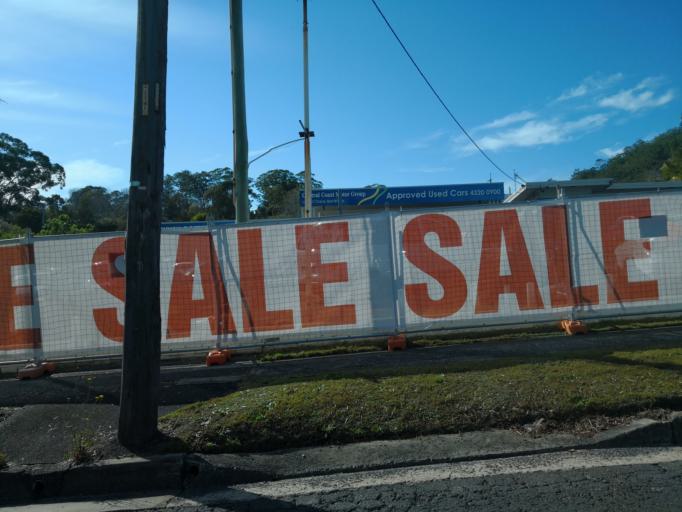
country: AU
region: New South Wales
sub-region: Gosford Shire
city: Gosford
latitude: -33.4188
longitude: 151.3435
